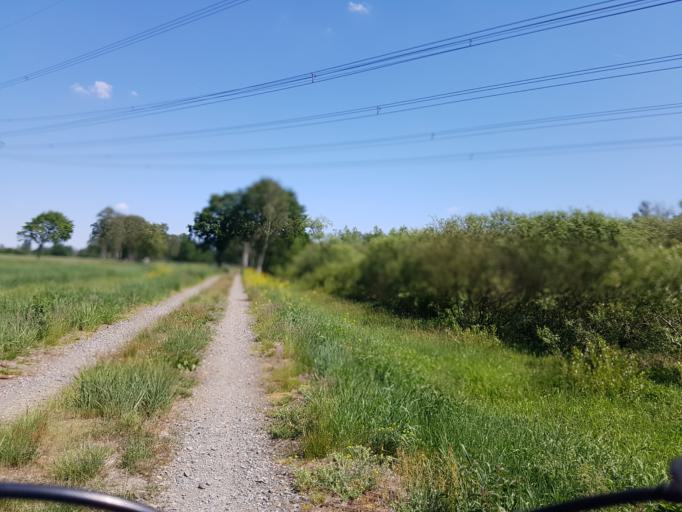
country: DE
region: Brandenburg
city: Merzdorf
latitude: 51.4297
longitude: 13.5499
